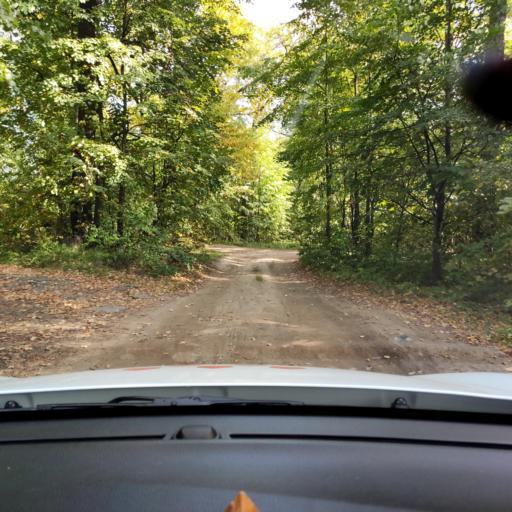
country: RU
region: Tatarstan
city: Staroye Arakchino
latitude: 55.8067
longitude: 49.0156
